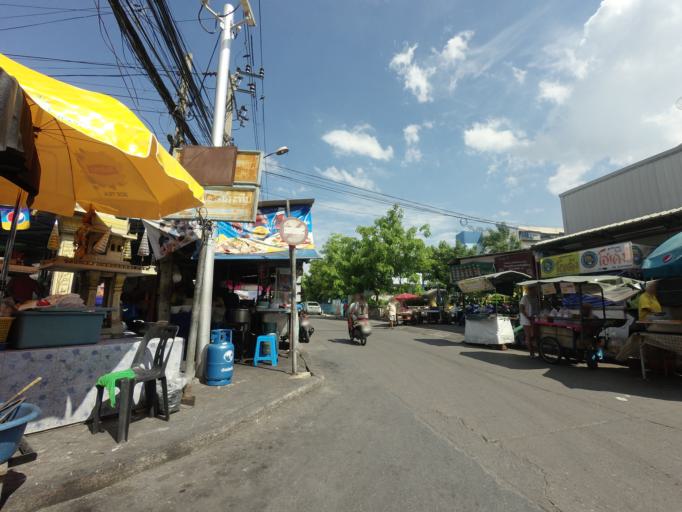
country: TH
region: Bangkok
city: Khlong Toei
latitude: 13.7116
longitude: 100.5703
